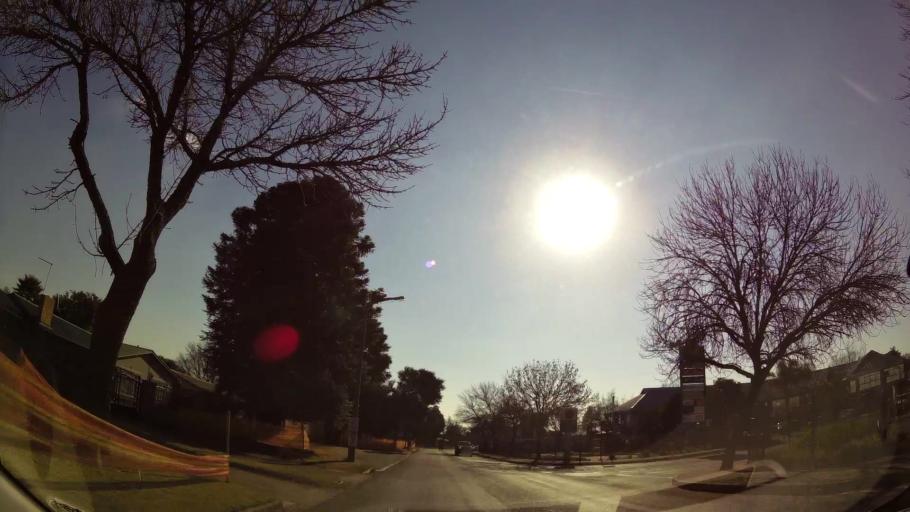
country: ZA
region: Gauteng
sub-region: Ekurhuleni Metropolitan Municipality
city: Benoni
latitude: -26.1494
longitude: 28.3097
